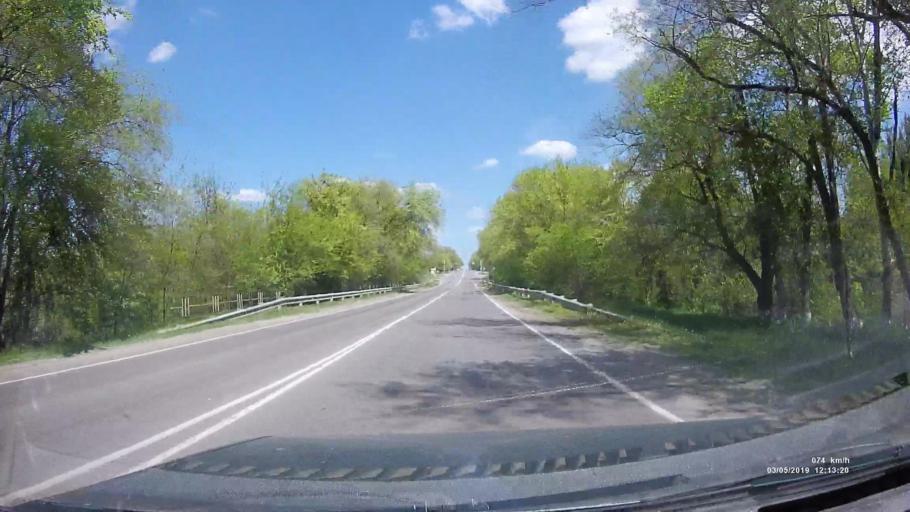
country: RU
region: Rostov
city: Melikhovskaya
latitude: 47.3315
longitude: 40.5541
